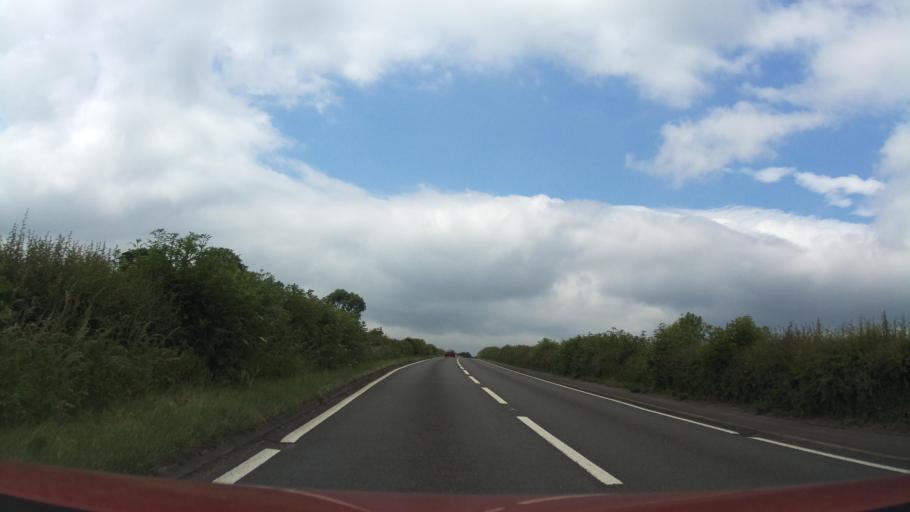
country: GB
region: England
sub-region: Derbyshire
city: Yeldersley
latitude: 52.9799
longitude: -1.6614
